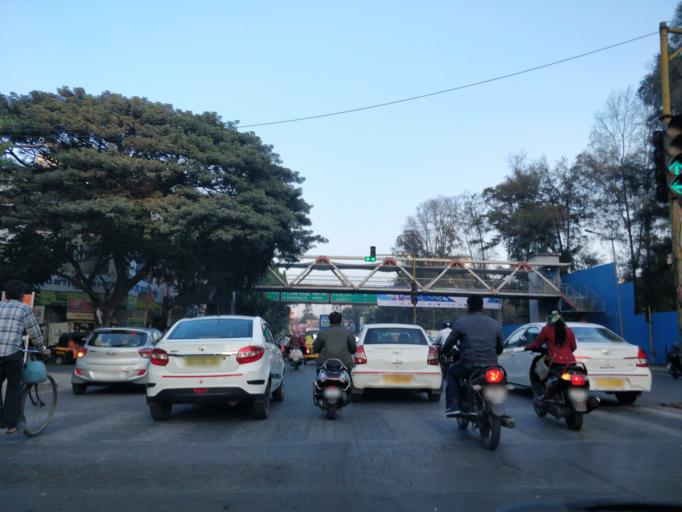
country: IN
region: Maharashtra
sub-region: Pune Division
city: Pune
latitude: 18.5028
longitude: 73.8182
